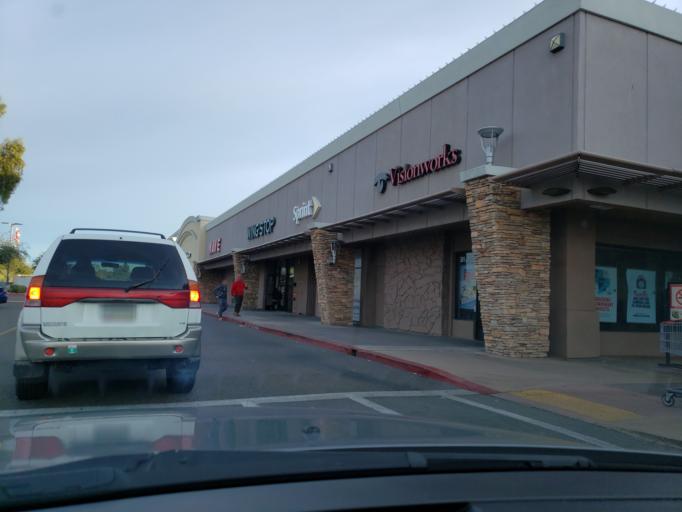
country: US
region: Arizona
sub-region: Maricopa County
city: Phoenix
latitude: 33.5228
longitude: -112.0954
